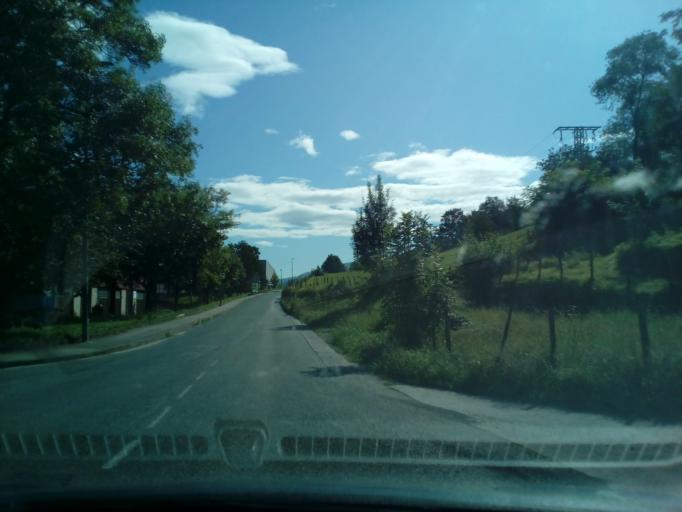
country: ES
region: Basque Country
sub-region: Provincia de Guipuzcoa
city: Aduna
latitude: 43.2034
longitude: -2.0437
